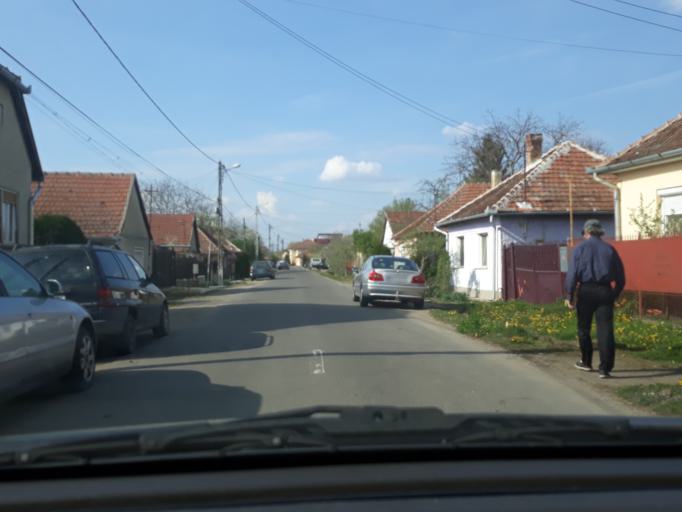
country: RO
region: Bihor
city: Margita
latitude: 47.3465
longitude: 22.3291
